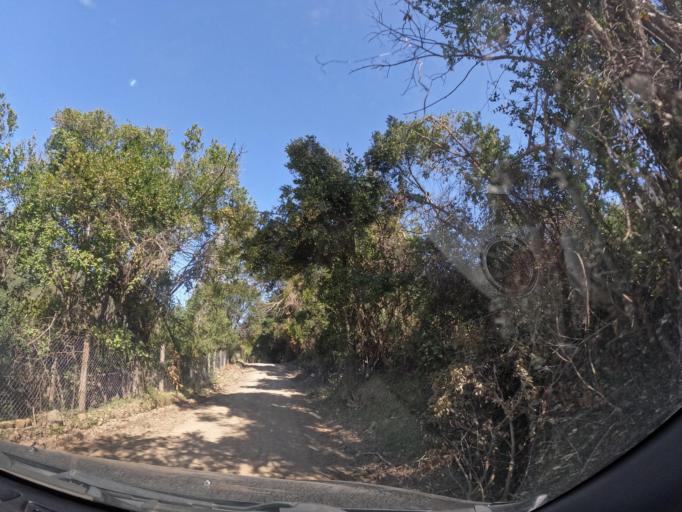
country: CL
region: Maule
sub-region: Provincia de Linares
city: Longavi
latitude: -36.2811
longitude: -71.4168
